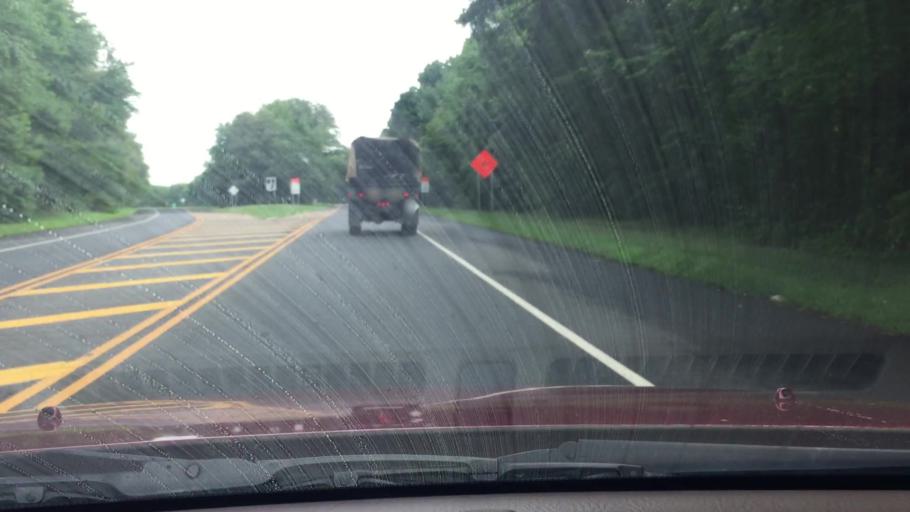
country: US
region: New Jersey
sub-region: Burlington County
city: Fort Dix
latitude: 40.0684
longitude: -74.6545
